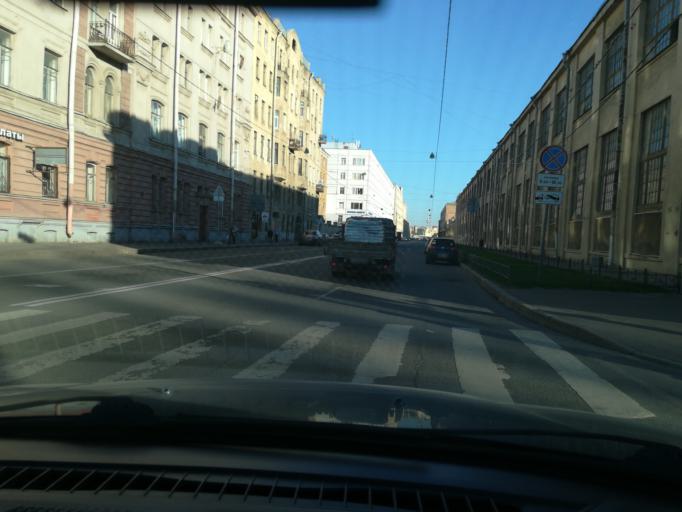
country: RU
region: St.-Petersburg
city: Vasyl'evsky Ostrov
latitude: 59.9328
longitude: 30.2628
